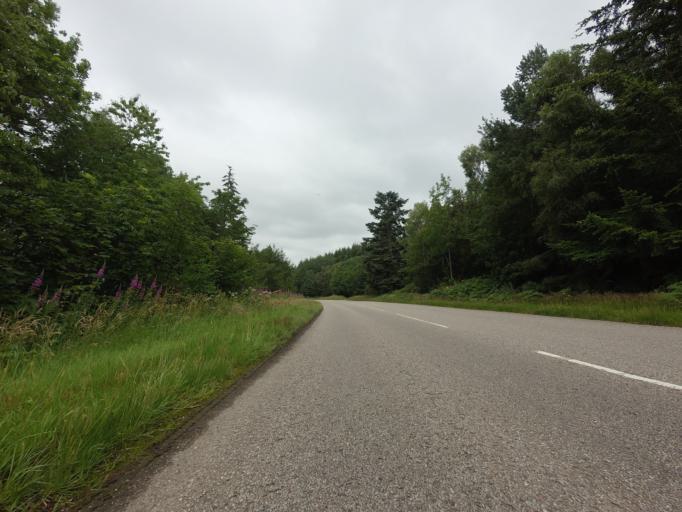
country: GB
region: Scotland
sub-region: Highland
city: Alness
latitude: 57.9064
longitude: -4.3609
